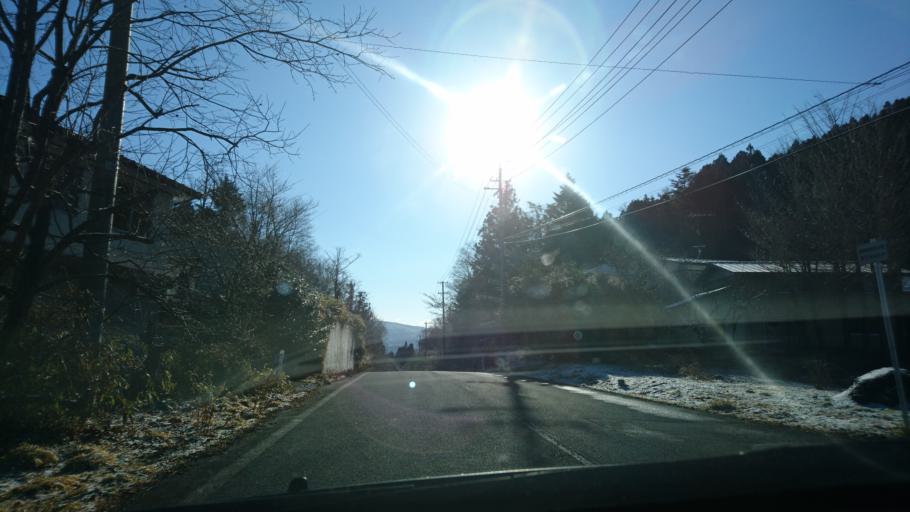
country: JP
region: Iwate
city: Ichinoseki
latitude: 38.8777
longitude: 141.3250
